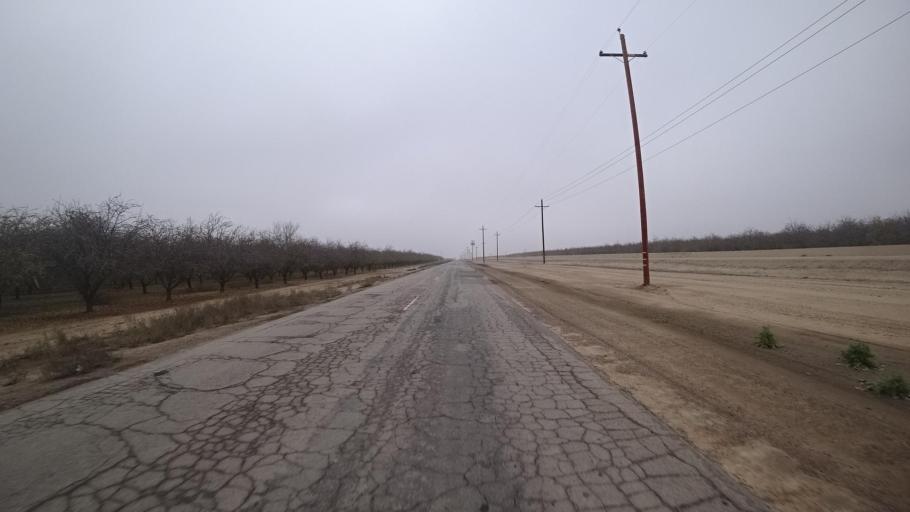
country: US
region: California
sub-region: Kern County
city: Wasco
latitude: 35.6921
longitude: -119.4012
